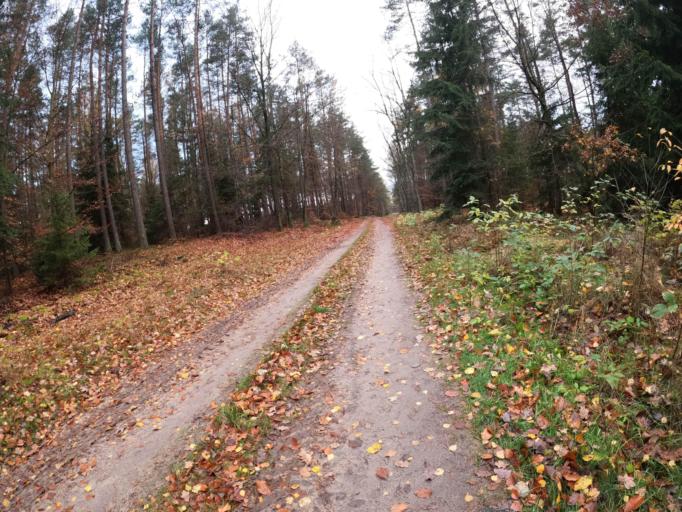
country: PL
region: West Pomeranian Voivodeship
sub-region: Powiat walecki
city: Tuczno
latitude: 53.2233
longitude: 16.2663
